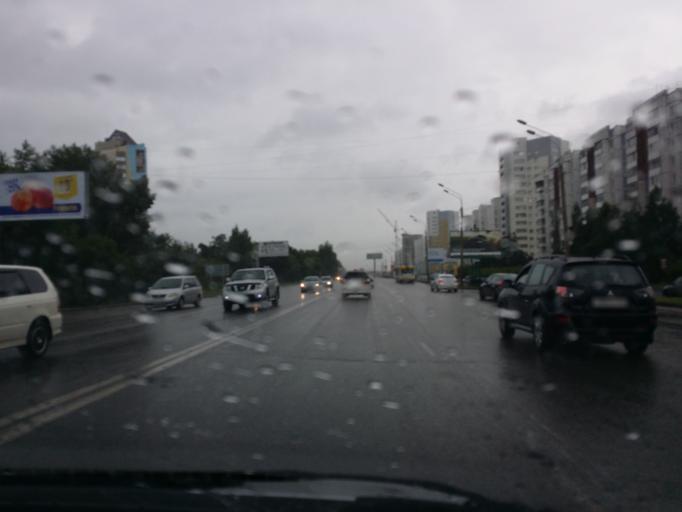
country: RU
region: Altai Krai
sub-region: Gorod Barnaulskiy
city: Barnaul
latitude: 53.3418
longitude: 83.6991
